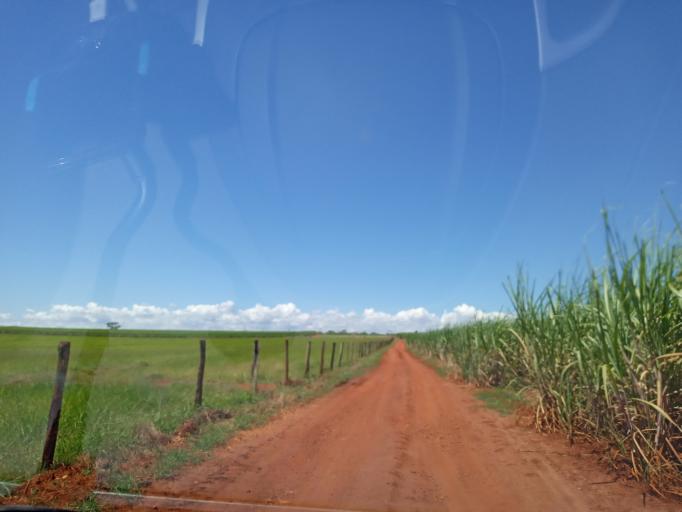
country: BR
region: Goias
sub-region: Itumbiara
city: Itumbiara
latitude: -18.4010
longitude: -49.1304
